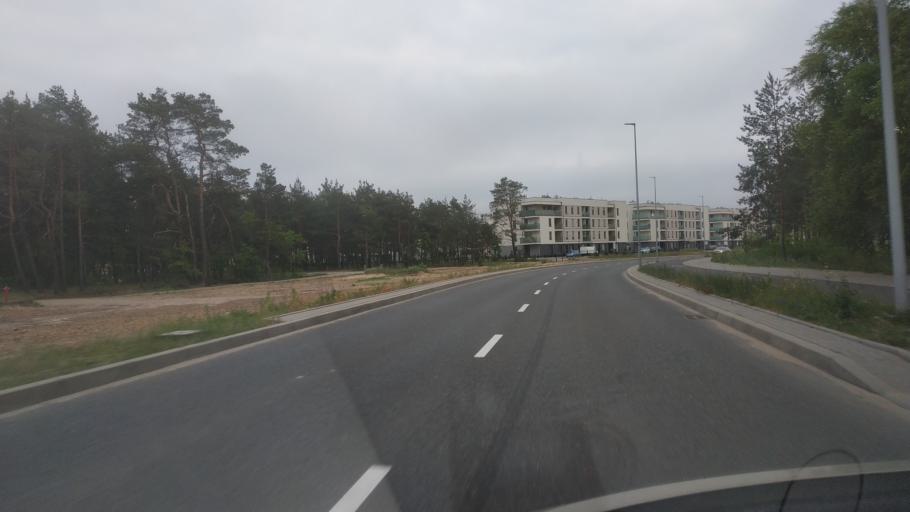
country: PL
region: Kujawsko-Pomorskie
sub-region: Torun
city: Torun
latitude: 53.0492
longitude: 18.6044
